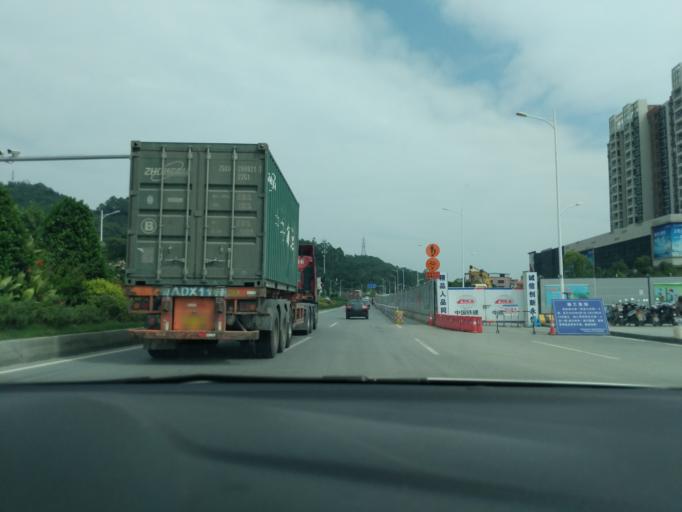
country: CN
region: Guangdong
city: Nansha
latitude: 22.7559
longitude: 113.5683
